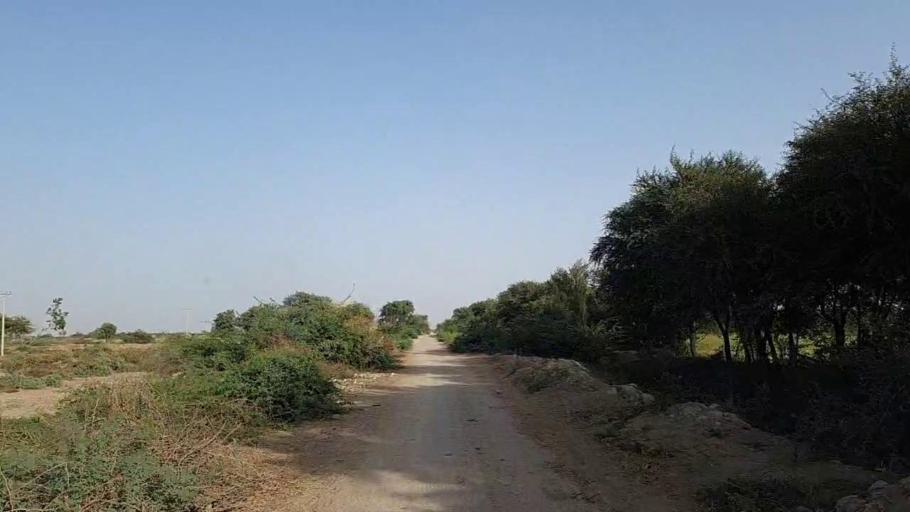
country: PK
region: Sindh
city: Jati
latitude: 24.2640
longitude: 68.1677
